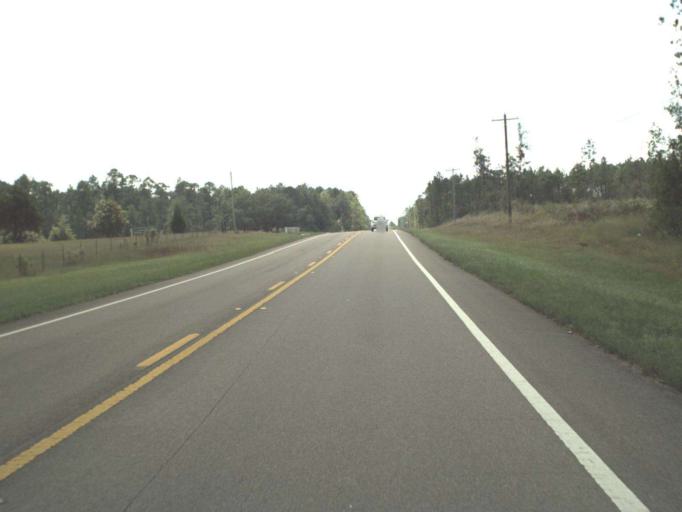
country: US
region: Florida
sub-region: Walton County
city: Freeport
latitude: 30.5317
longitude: -85.9231
